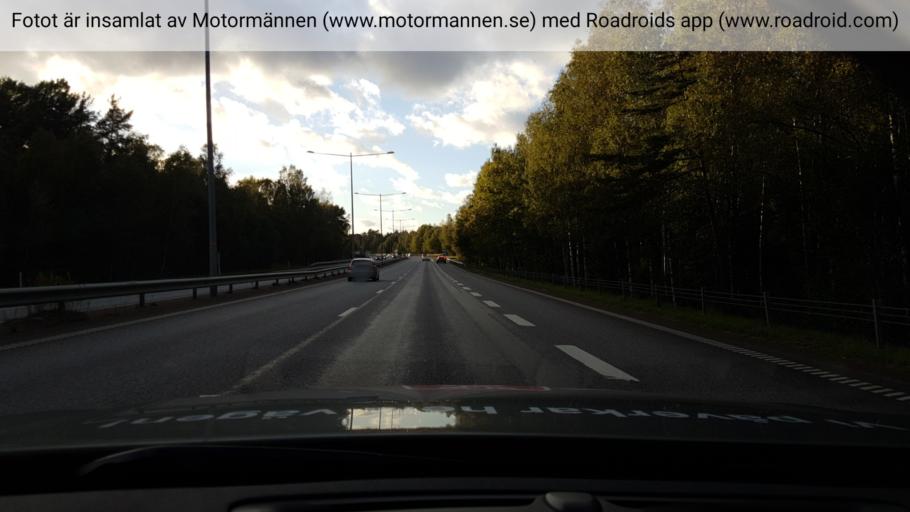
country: SE
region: Vaermland
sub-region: Karlstads Kommun
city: Karlstad
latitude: 59.3999
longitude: 13.5613
